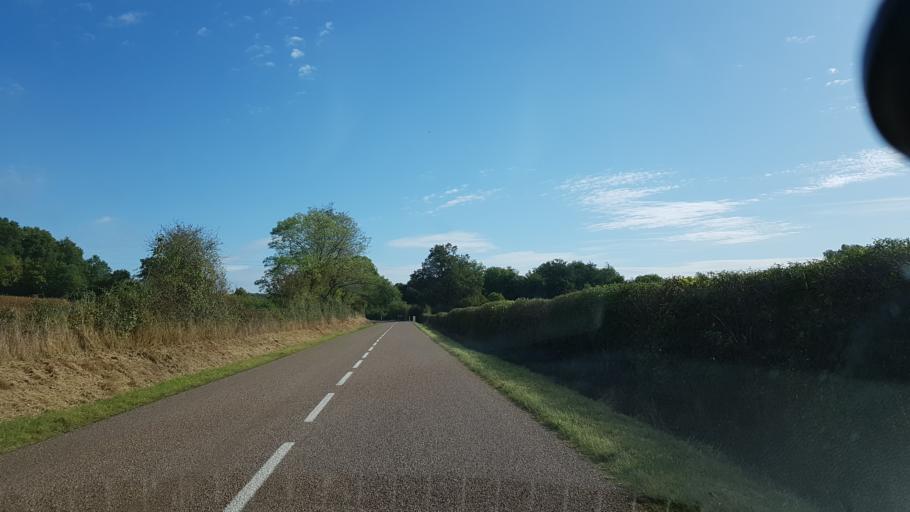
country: FR
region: Bourgogne
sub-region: Departement de la Nievre
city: Neuvy-sur-Loire
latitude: 47.5305
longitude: 2.8914
